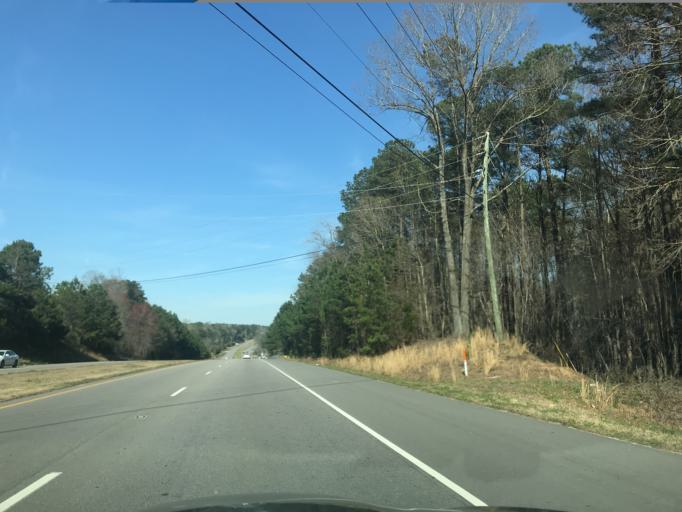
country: US
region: North Carolina
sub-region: Wake County
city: Fuquay-Varina
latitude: 35.6118
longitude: -78.7403
